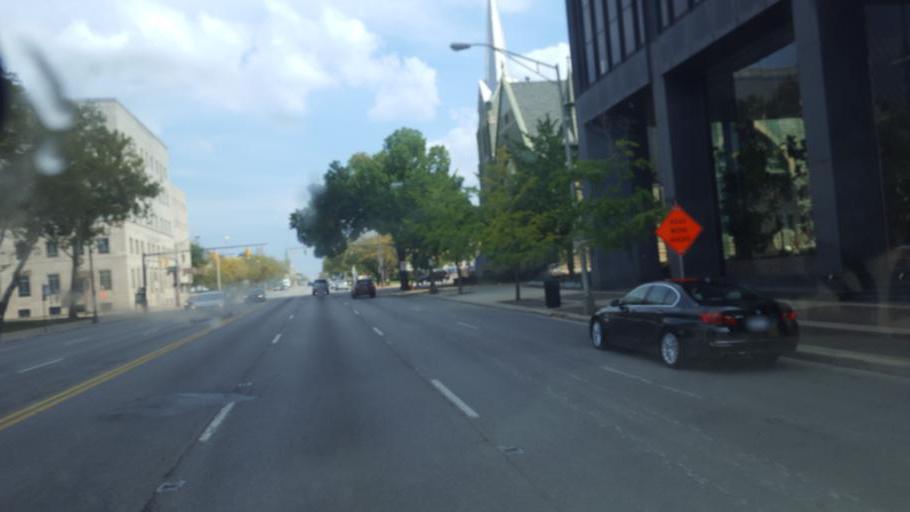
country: US
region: Ohio
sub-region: Franklin County
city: Columbus
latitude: 39.9636
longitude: -82.9882
